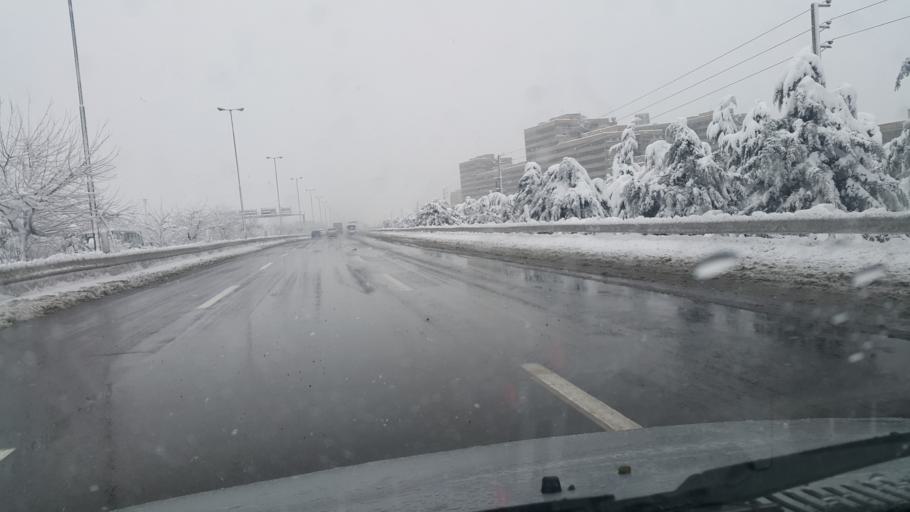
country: IR
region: Tehran
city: Tehran
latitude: 35.7165
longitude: 51.3149
